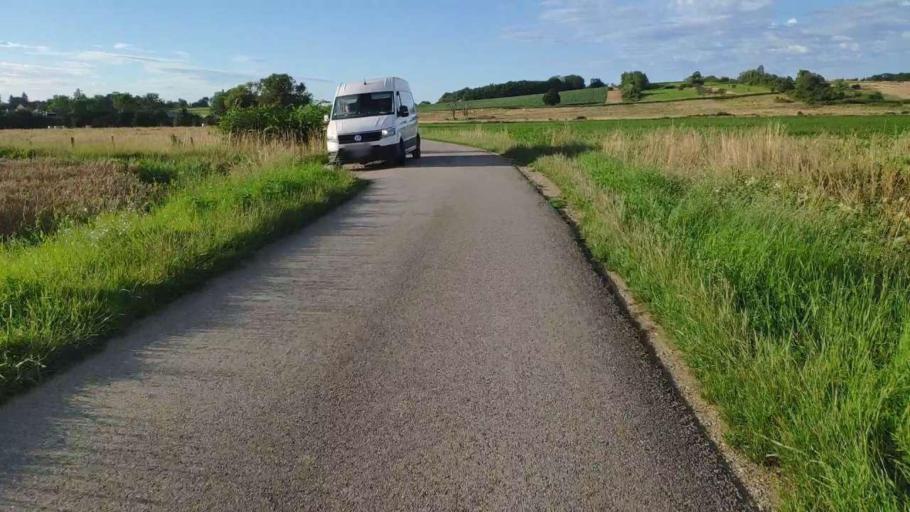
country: FR
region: Franche-Comte
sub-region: Departement du Jura
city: Bletterans
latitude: 46.7739
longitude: 5.4963
